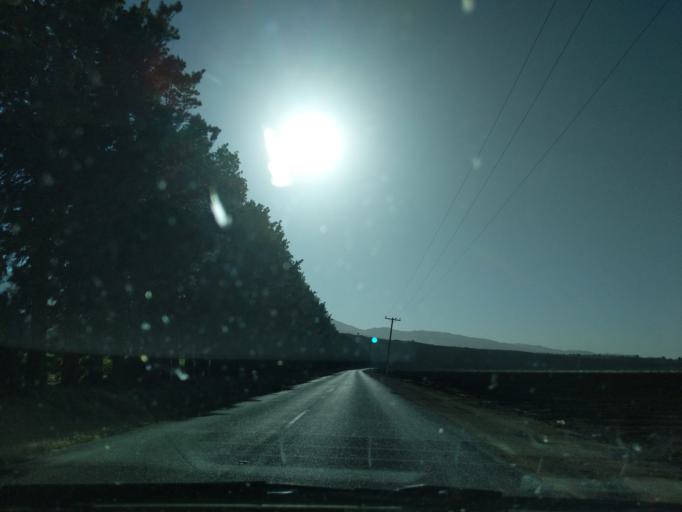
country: US
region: California
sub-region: Monterey County
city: Soledad
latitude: 36.4104
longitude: -121.3837
